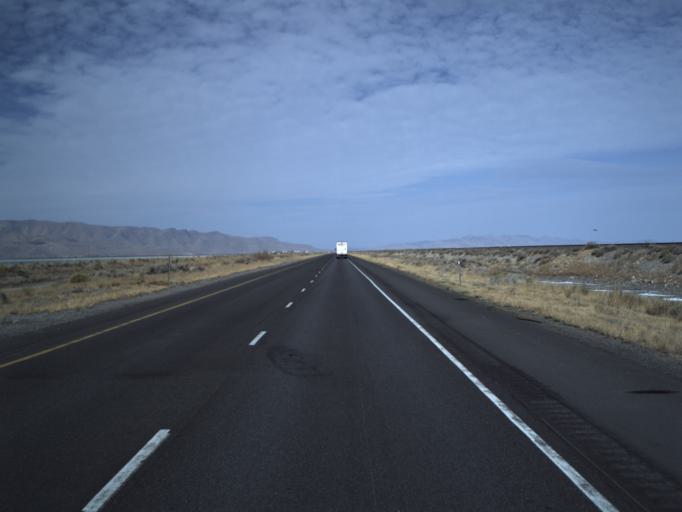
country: US
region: Utah
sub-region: Tooele County
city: Stansbury park
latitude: 40.6693
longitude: -112.3792
